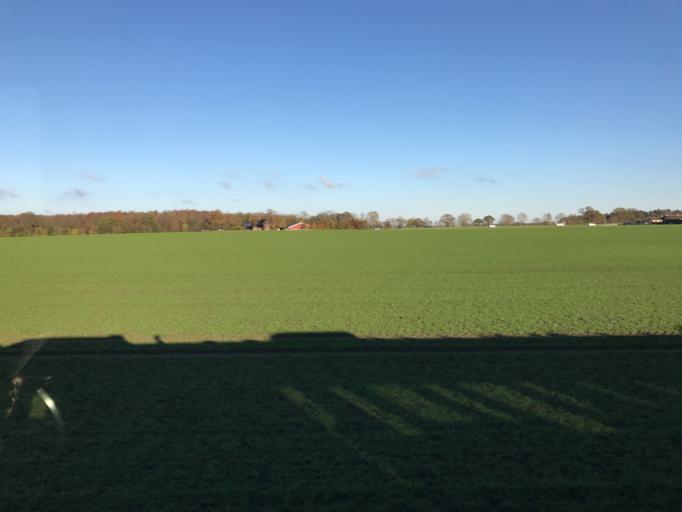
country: DK
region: Zealand
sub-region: Stevns Kommune
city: Store Heddinge
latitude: 55.3361
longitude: 12.3441
